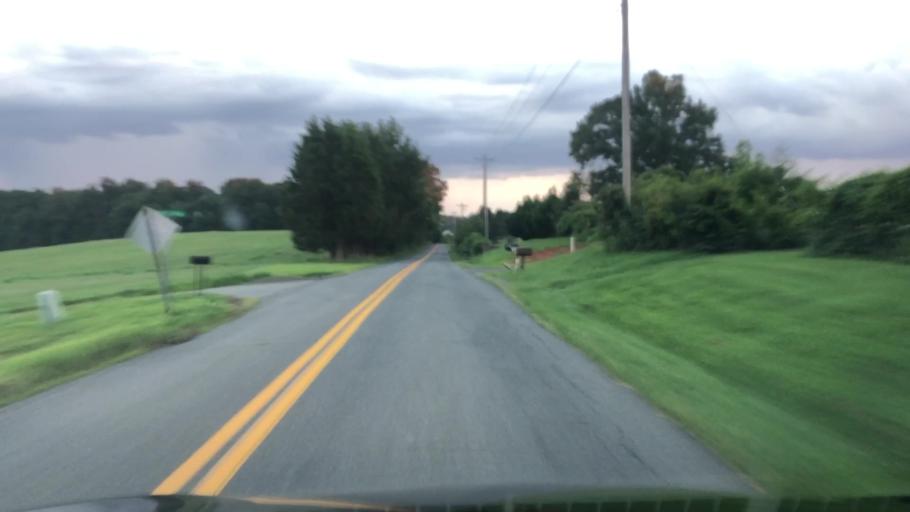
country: US
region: Virginia
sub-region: Stafford County
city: Stafford
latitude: 38.4704
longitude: -77.5790
